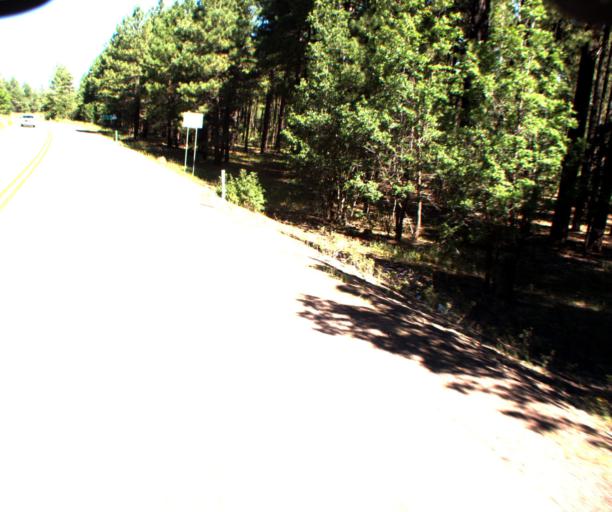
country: US
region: Arizona
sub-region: Navajo County
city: Pinetop-Lakeside
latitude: 34.0765
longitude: -109.8647
